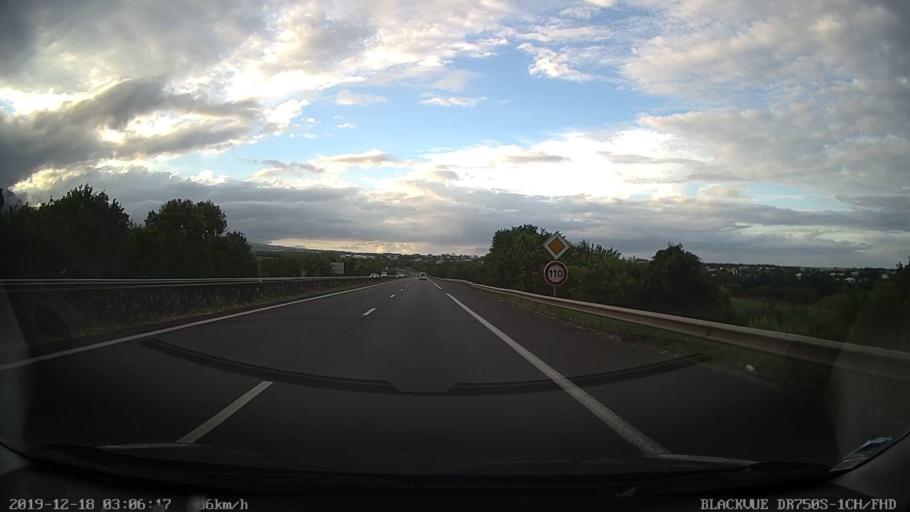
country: RE
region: Reunion
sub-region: Reunion
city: Bras-Panon
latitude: -21.0114
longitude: 55.6888
